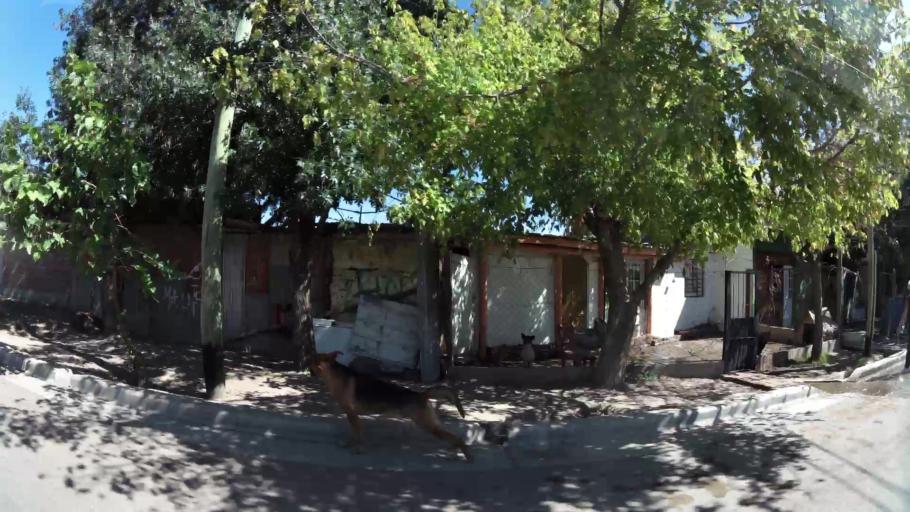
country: AR
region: Mendoza
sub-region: Departamento de Godoy Cruz
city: Godoy Cruz
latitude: -32.9658
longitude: -68.8414
